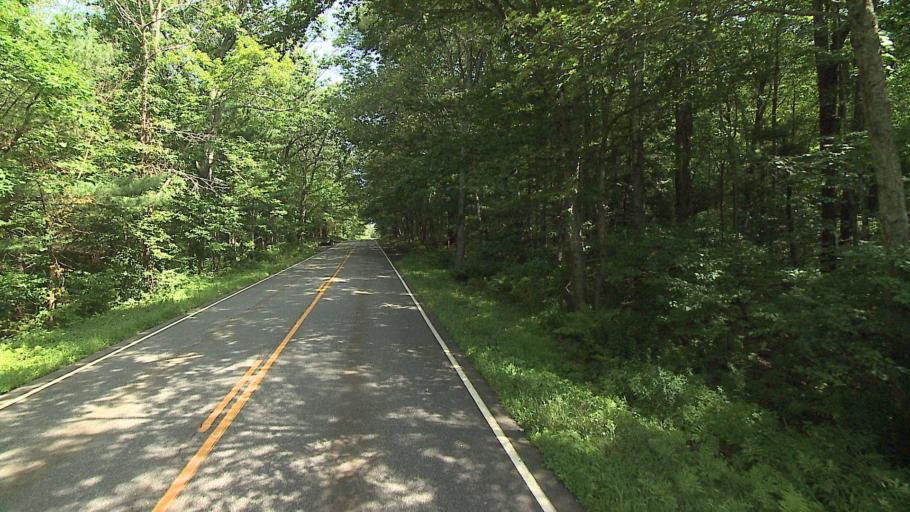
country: US
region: Connecticut
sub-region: Litchfield County
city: Litchfield
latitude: 41.6990
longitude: -73.1920
